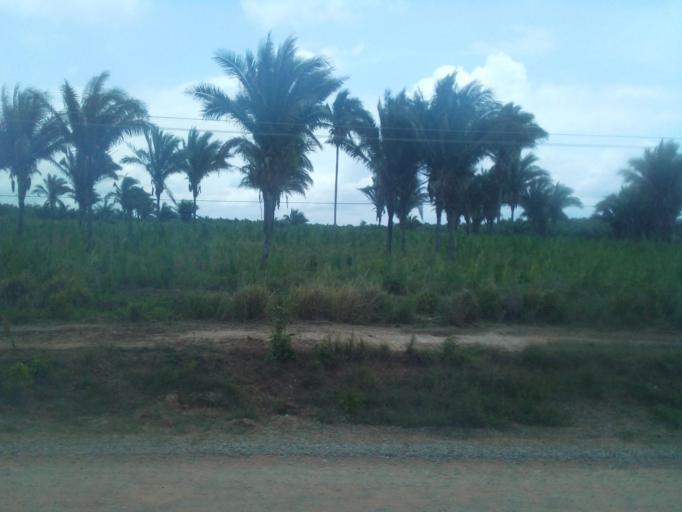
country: BR
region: Maranhao
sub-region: Santa Ines
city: Santa Ines
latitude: -3.7206
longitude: -45.5163
